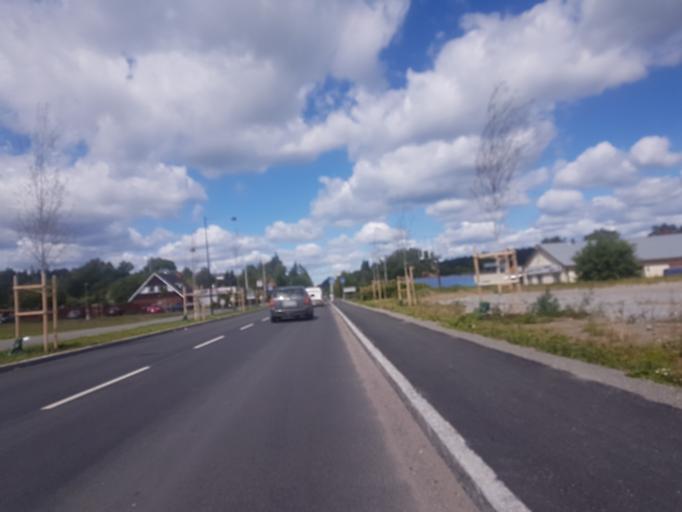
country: SE
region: Soedermanland
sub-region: Gnesta Kommun
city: Gnesta
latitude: 59.0411
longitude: 17.3270
